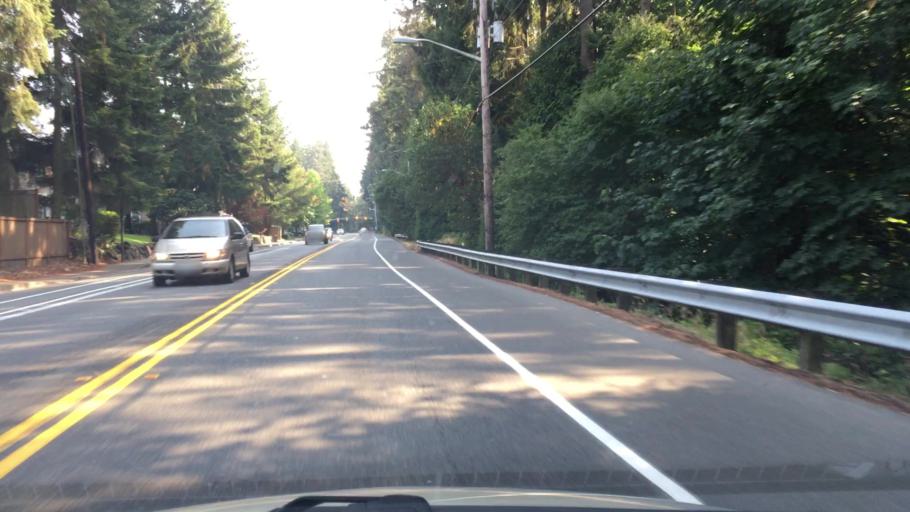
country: US
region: Washington
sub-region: King County
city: Inglewood-Finn Hill
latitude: 47.7310
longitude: -122.2451
